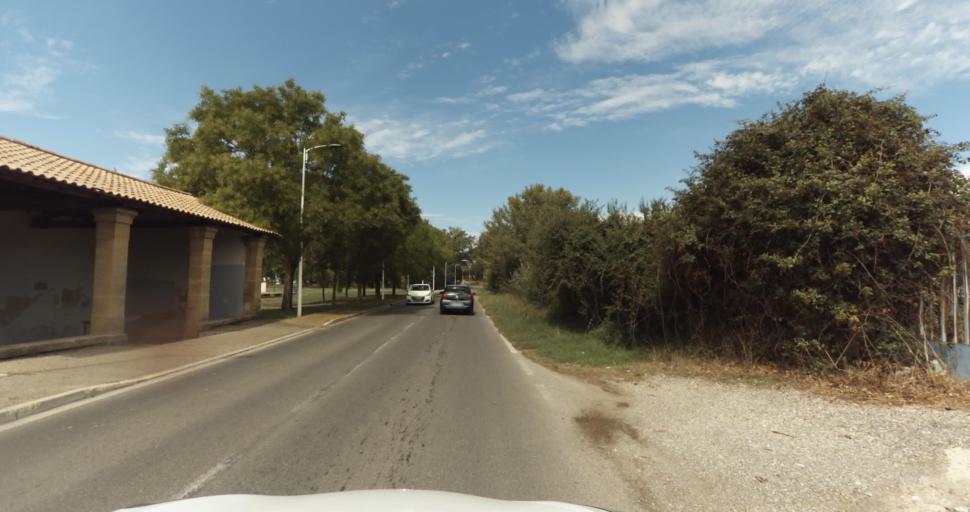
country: FR
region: Provence-Alpes-Cote d'Azur
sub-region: Departement des Bouches-du-Rhone
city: Miramas
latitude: 43.5905
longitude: 5.0137
